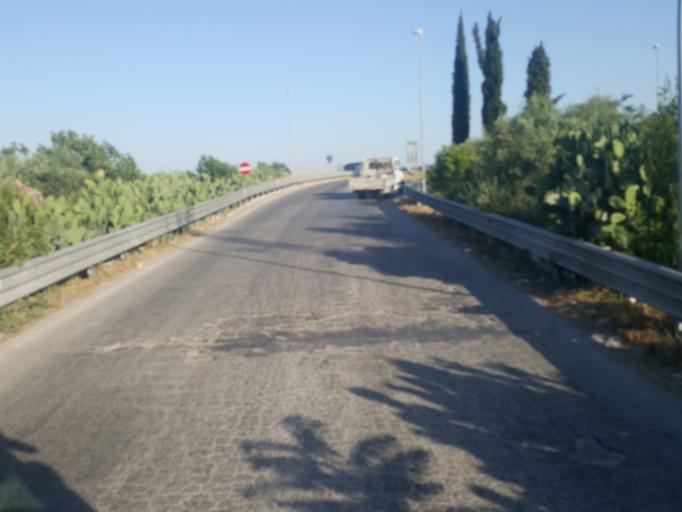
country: IT
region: Apulia
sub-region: Provincia di Foggia
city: Cerignola
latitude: 41.2802
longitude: 15.8950
